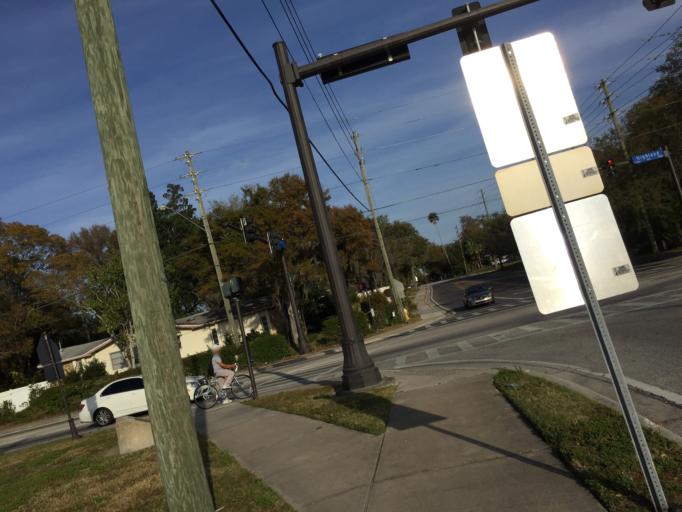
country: US
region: Florida
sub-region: Pinellas County
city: Clearwater
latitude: 27.9755
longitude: -82.7756
